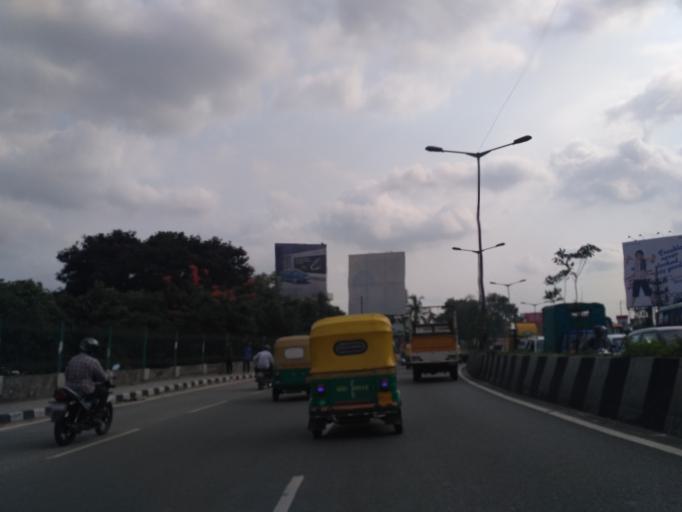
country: IN
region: Karnataka
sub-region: Bangalore Urban
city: Bangalore
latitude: 12.9585
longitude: 77.5552
